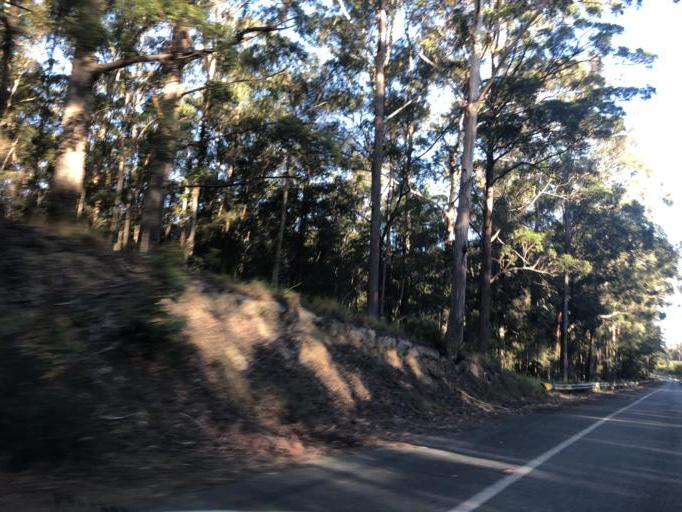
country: AU
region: New South Wales
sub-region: Nambucca Shire
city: Nambucca
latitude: -30.5541
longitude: 153.0069
